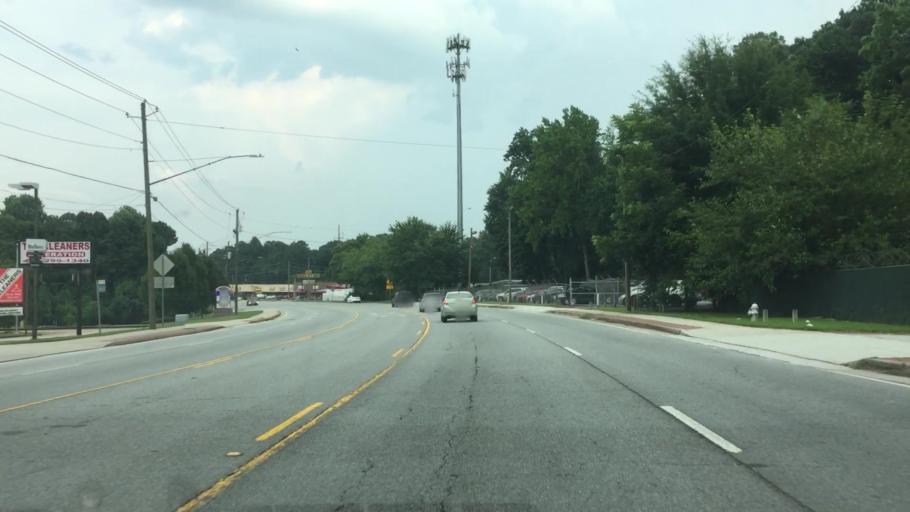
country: US
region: Georgia
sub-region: DeKalb County
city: Avondale Estates
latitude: 33.7633
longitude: -84.2505
